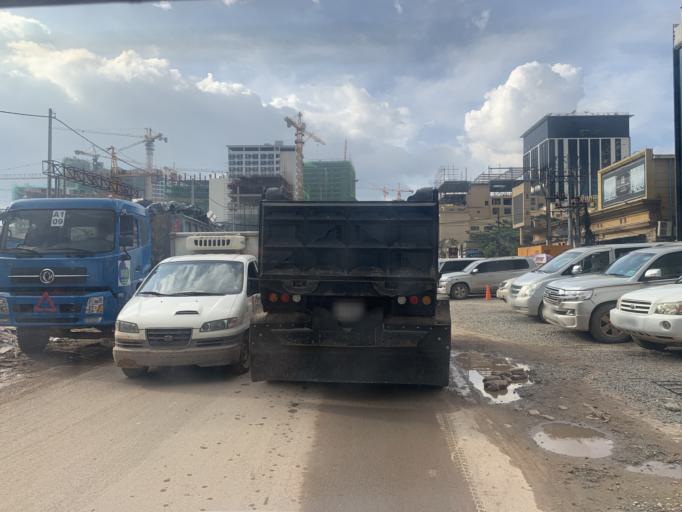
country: KH
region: Preah Sihanouk
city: Sihanoukville
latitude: 10.6072
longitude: 103.5256
